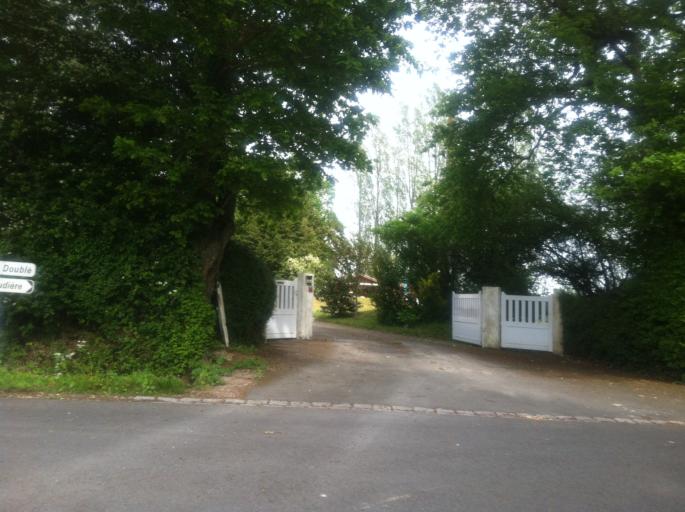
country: FR
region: Brittany
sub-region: Departement d'Ille-et-Vilaine
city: Chartres-de-Bretagne
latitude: 48.0355
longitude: -1.7201
